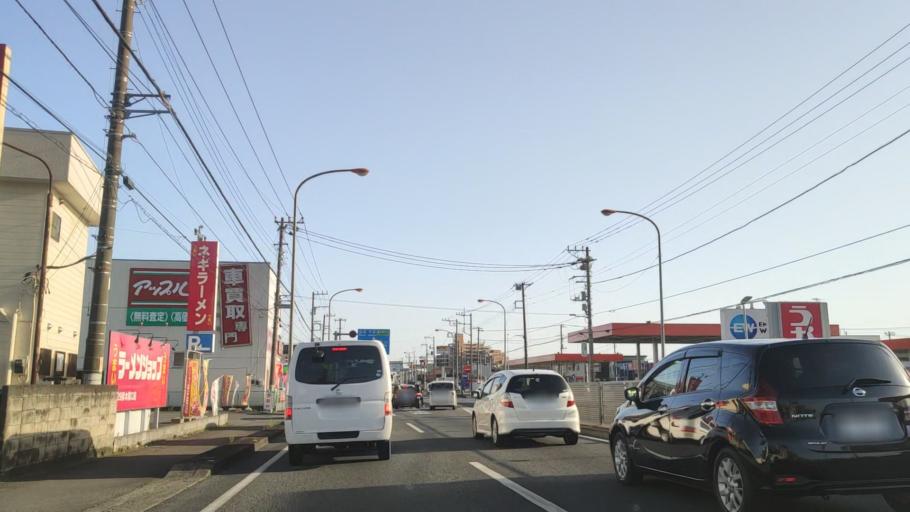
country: JP
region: Kanagawa
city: Zama
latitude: 35.4881
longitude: 139.3648
